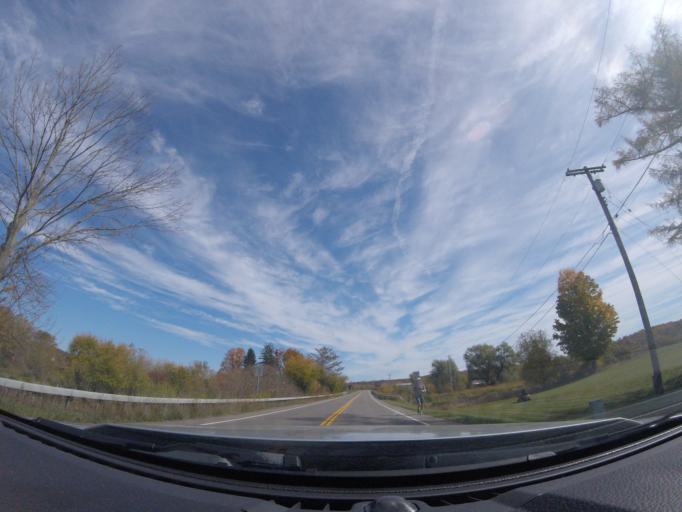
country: US
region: New York
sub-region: Tompkins County
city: Dryden
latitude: 42.5173
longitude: -76.3397
